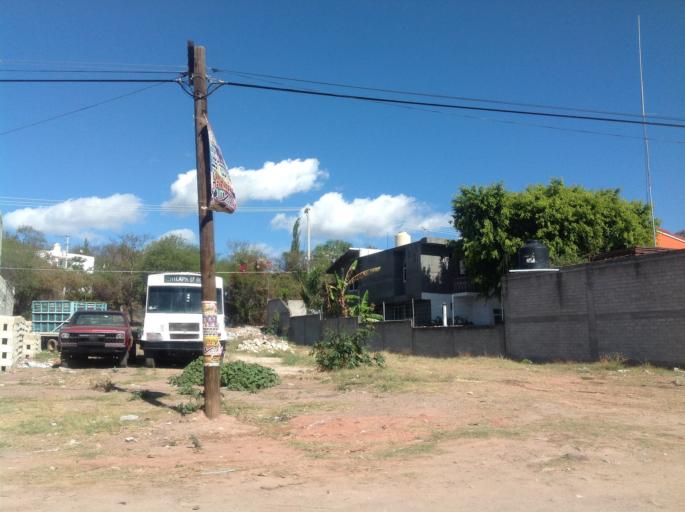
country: MX
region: Oaxaca
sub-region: Heroica Ciudad de Huajuapan de Leon
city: Vista Hermosa
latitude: 17.8148
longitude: -97.7614
